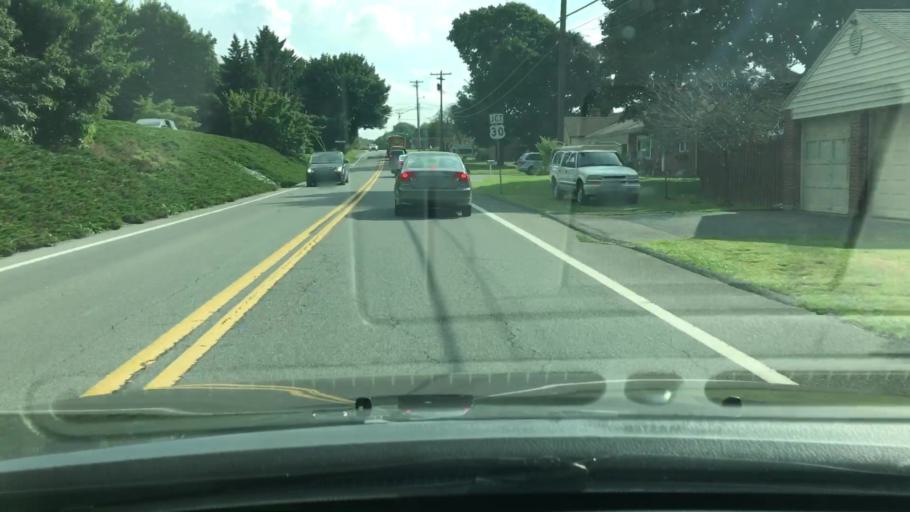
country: US
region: Pennsylvania
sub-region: Franklin County
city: Guilford
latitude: 39.9227
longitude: -77.5921
